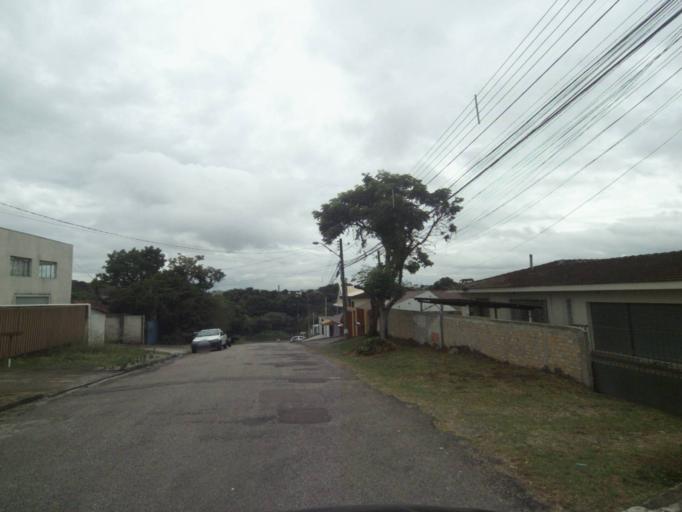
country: BR
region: Parana
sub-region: Curitiba
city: Curitiba
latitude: -25.4751
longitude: -49.3314
